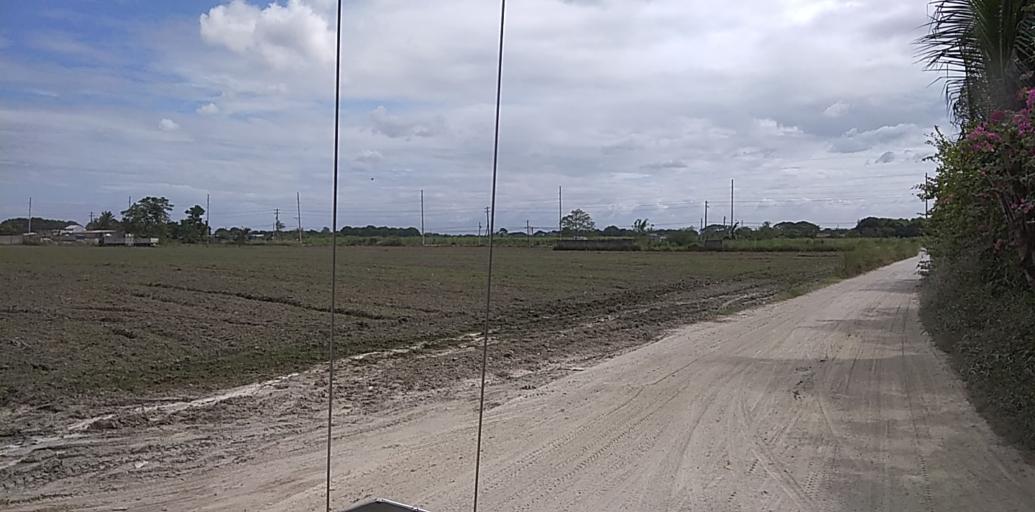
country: PH
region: Central Luzon
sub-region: Province of Pampanga
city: Porac
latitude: 15.0568
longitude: 120.5354
